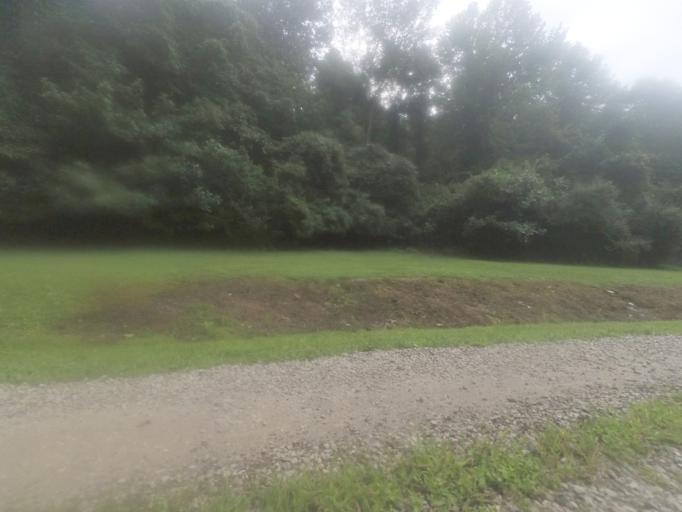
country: US
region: West Virginia
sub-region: Cabell County
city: Huntington
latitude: 38.3770
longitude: -82.3941
